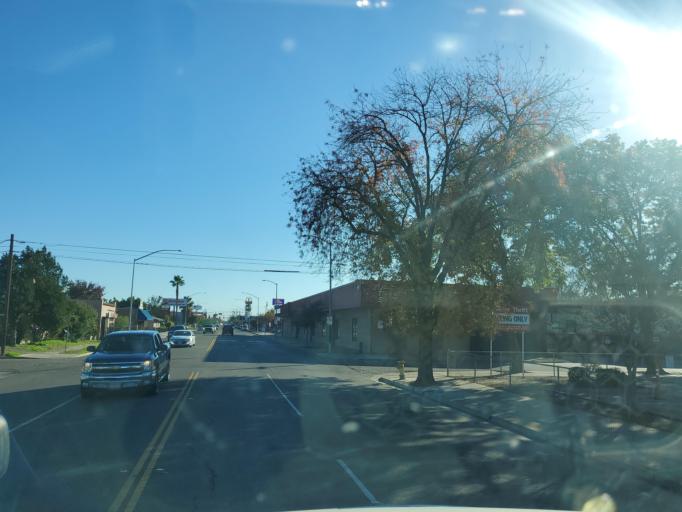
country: US
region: California
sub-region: San Joaquin County
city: August
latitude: 37.9692
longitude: -121.2752
